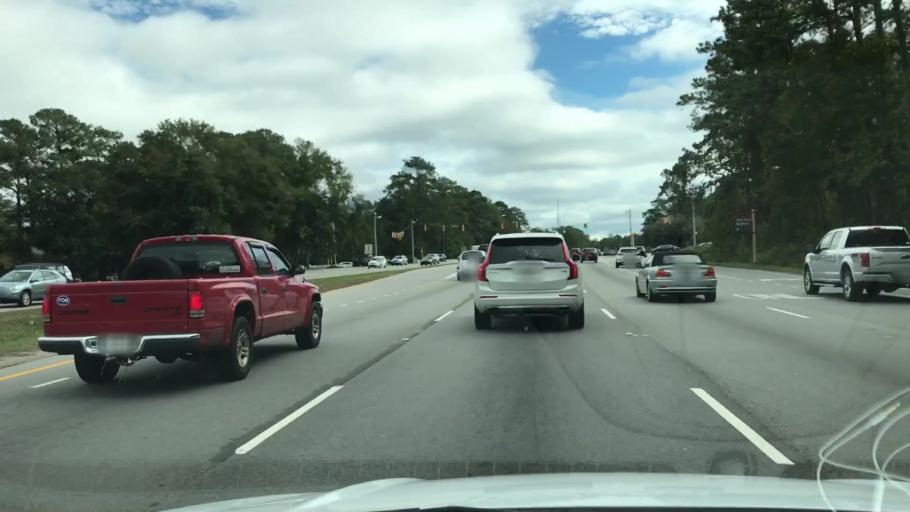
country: US
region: South Carolina
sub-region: Beaufort County
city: Bluffton
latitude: 32.2614
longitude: -80.8538
